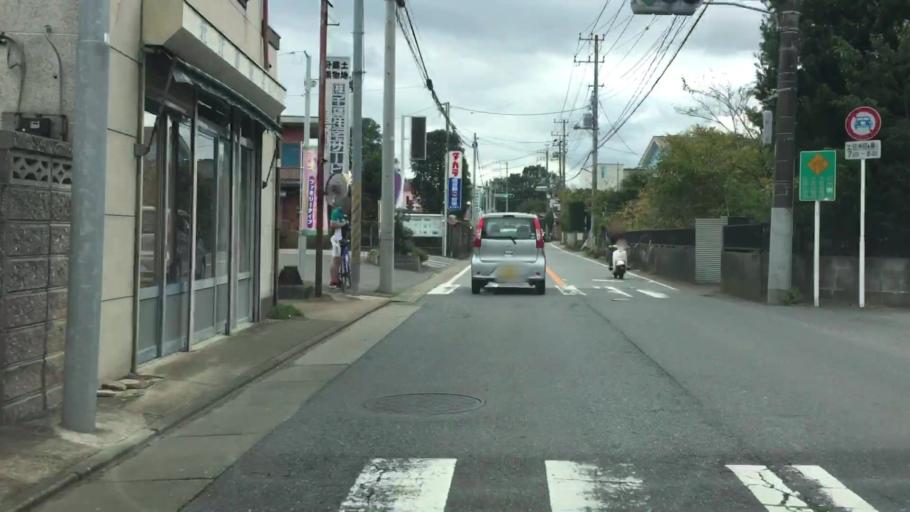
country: JP
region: Ibaraki
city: Ryugasaki
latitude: 35.8368
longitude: 140.1437
